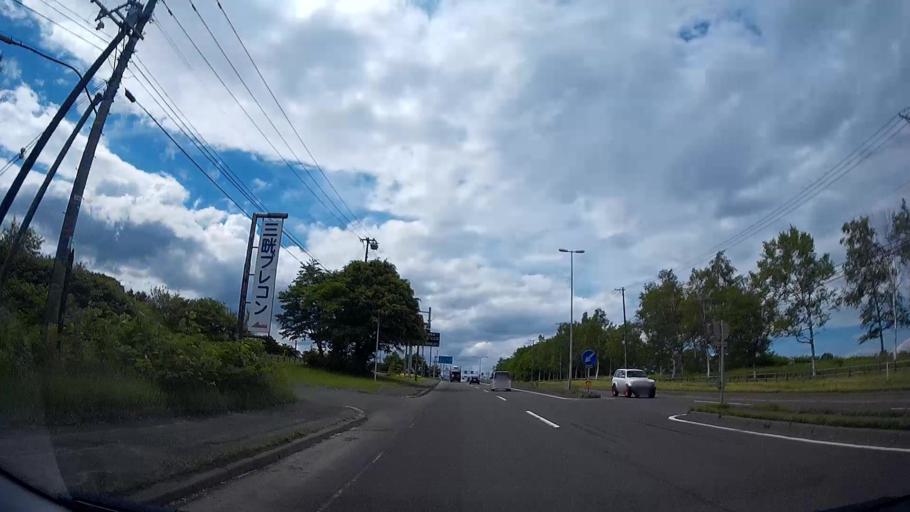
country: JP
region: Hokkaido
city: Chitose
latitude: 42.8586
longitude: 141.6036
